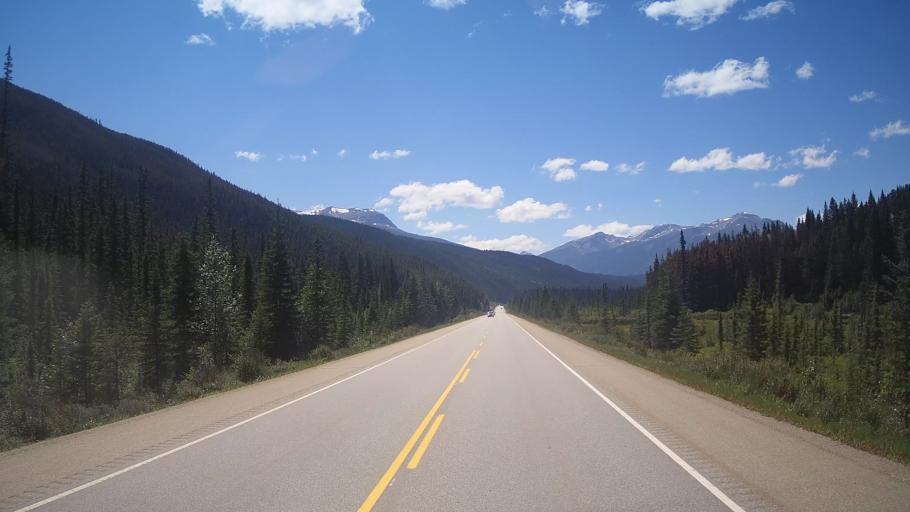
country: CA
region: Alberta
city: Jasper Park Lodge
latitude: 52.8845
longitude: -118.4851
